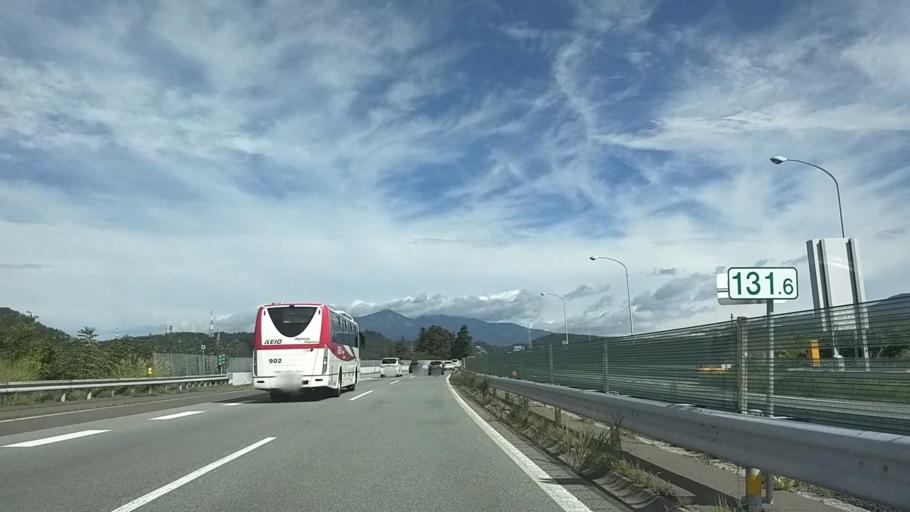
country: JP
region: Yamanashi
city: Nirasaki
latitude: 35.7742
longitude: 138.4231
